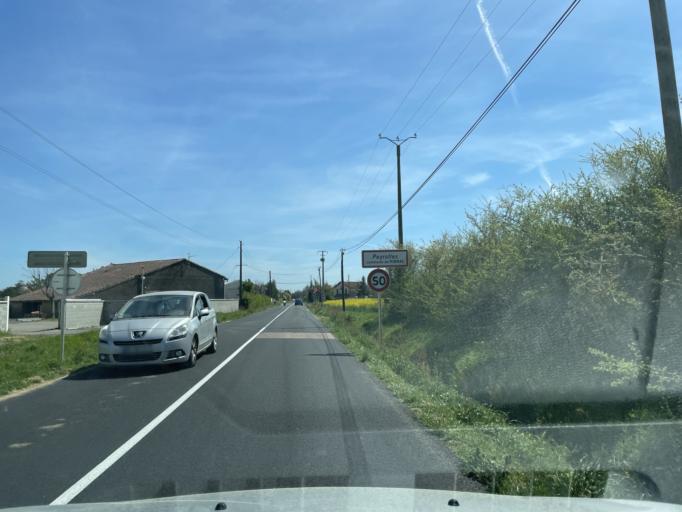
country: FR
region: Midi-Pyrenees
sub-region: Departement de la Haute-Garonne
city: Brax
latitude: 43.6242
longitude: 1.2455
